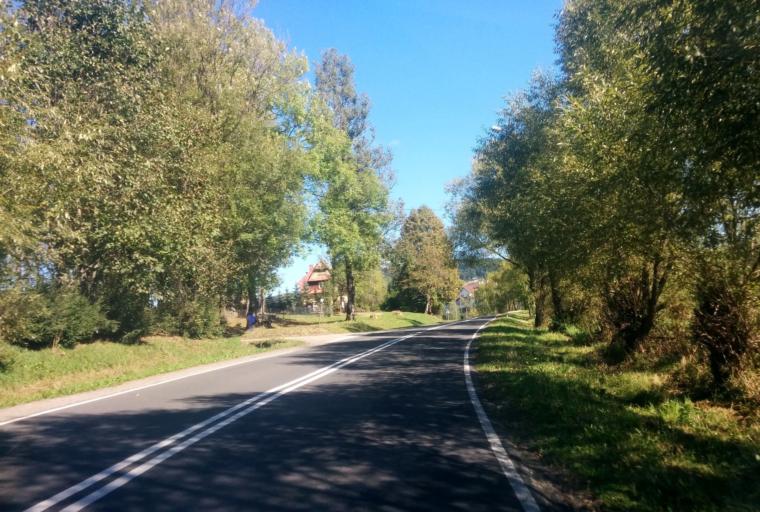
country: PL
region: Subcarpathian Voivodeship
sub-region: Powiat bieszczadzki
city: Lutowiska
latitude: 49.2474
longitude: 22.6938
